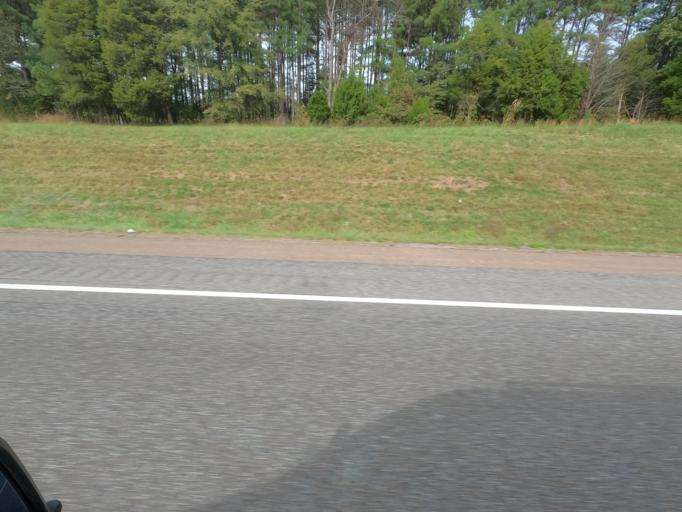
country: US
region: Tennessee
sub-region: Henderson County
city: Lexington
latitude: 35.7797
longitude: -88.4204
